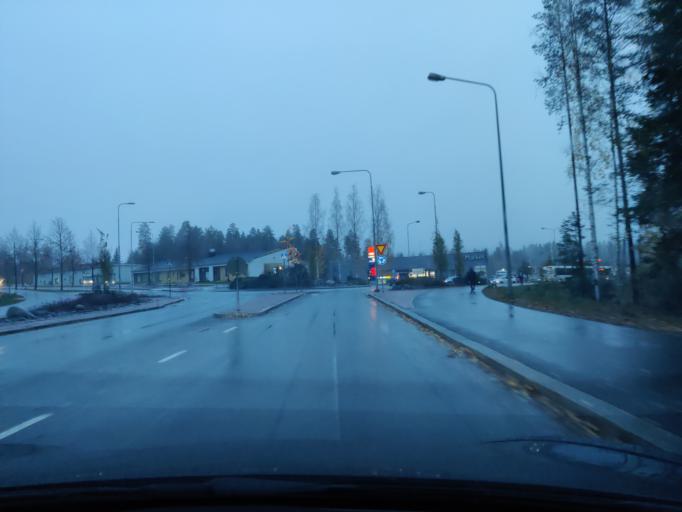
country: FI
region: Northern Savo
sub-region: Kuopio
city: Kuopio
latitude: 62.8335
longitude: 27.6668
